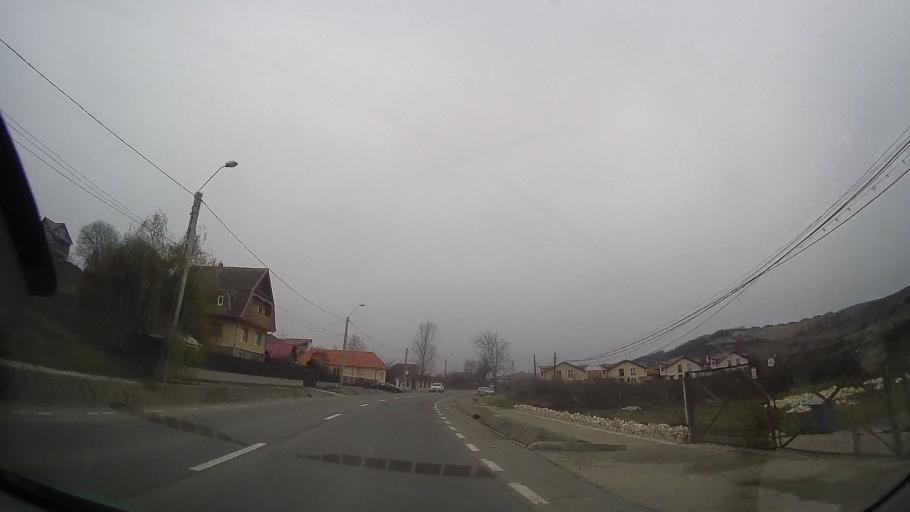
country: RO
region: Mures
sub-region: Comuna Ceausu de Campie
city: Ceausu de Campie
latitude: 46.6058
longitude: 24.5297
